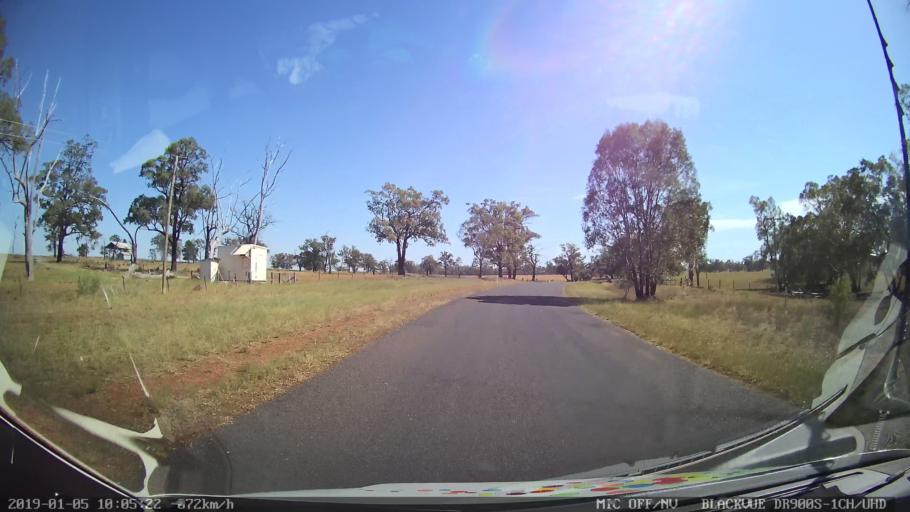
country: AU
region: New South Wales
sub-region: Gilgandra
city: Gilgandra
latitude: -31.6665
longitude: 148.8652
